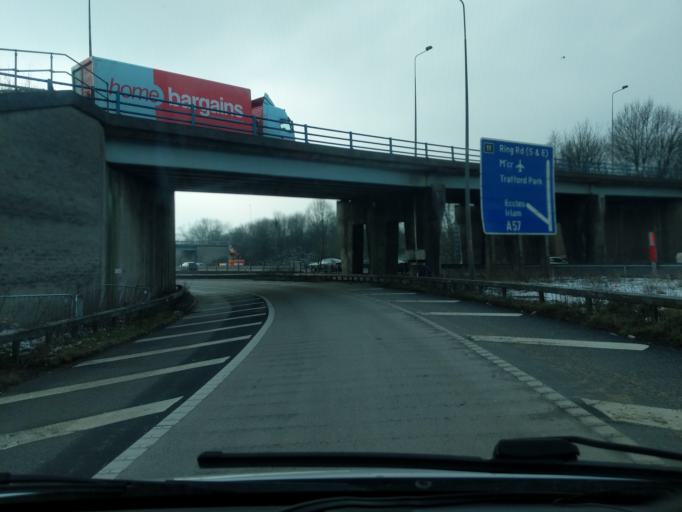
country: GB
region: England
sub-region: Manchester
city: Swinton
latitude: 53.4869
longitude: -2.3755
